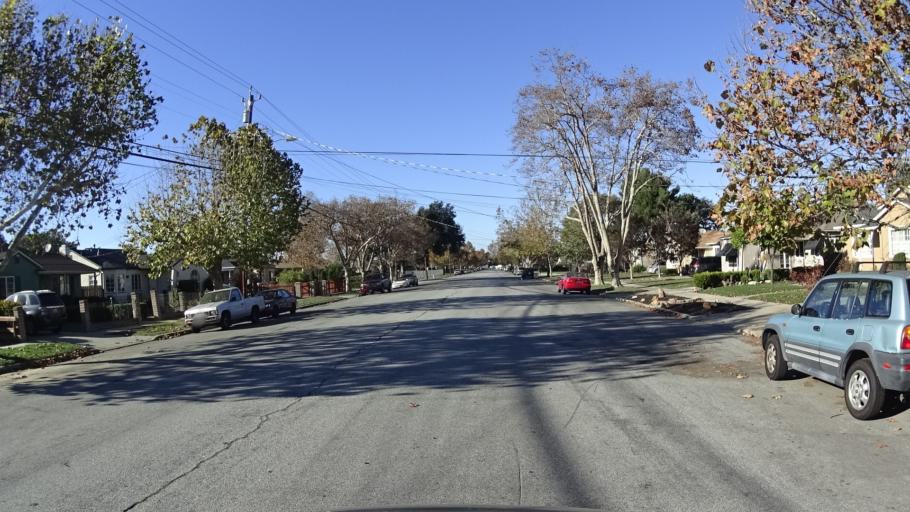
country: US
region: California
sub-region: Santa Clara County
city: San Jose
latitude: 37.3564
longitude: -121.8999
